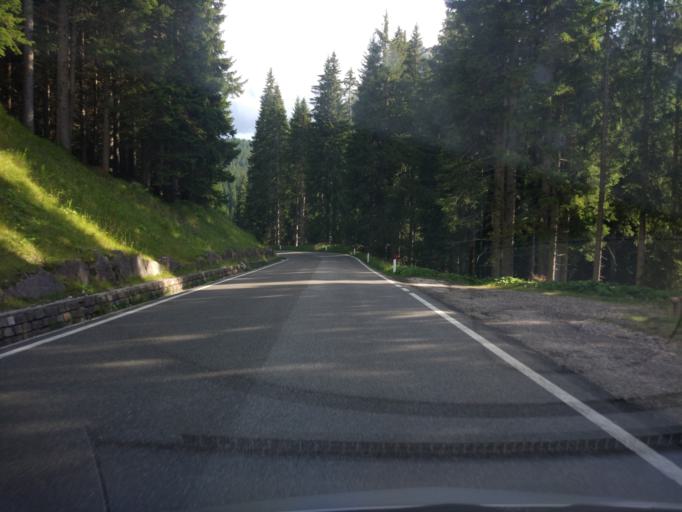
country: IT
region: Veneto
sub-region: Provincia di Belluno
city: Falcade Alto
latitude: 46.2994
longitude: 11.7633
